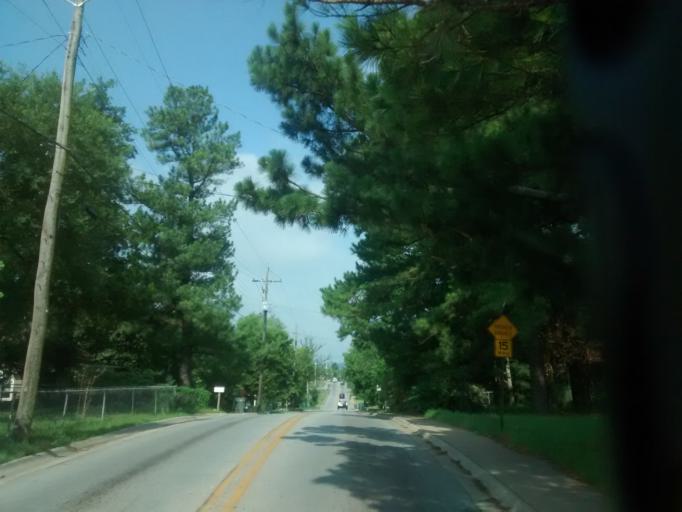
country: US
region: Arkansas
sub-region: Washington County
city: Fayetteville
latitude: 36.0562
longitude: -94.1537
